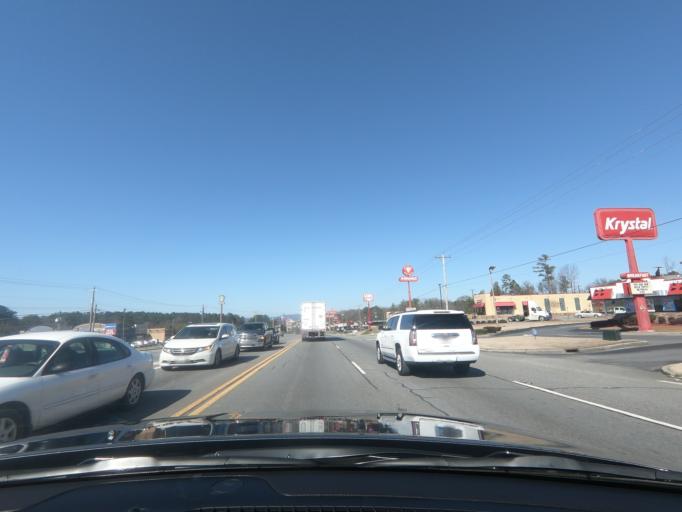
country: US
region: Georgia
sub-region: Gordon County
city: Calhoun
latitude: 34.4734
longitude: -84.9236
